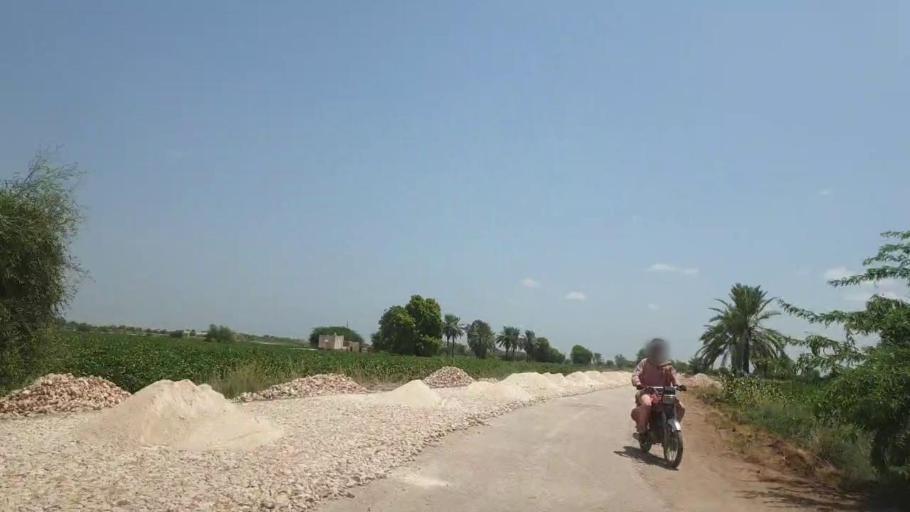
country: PK
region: Sindh
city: Pano Aqil
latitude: 27.6660
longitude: 69.1766
